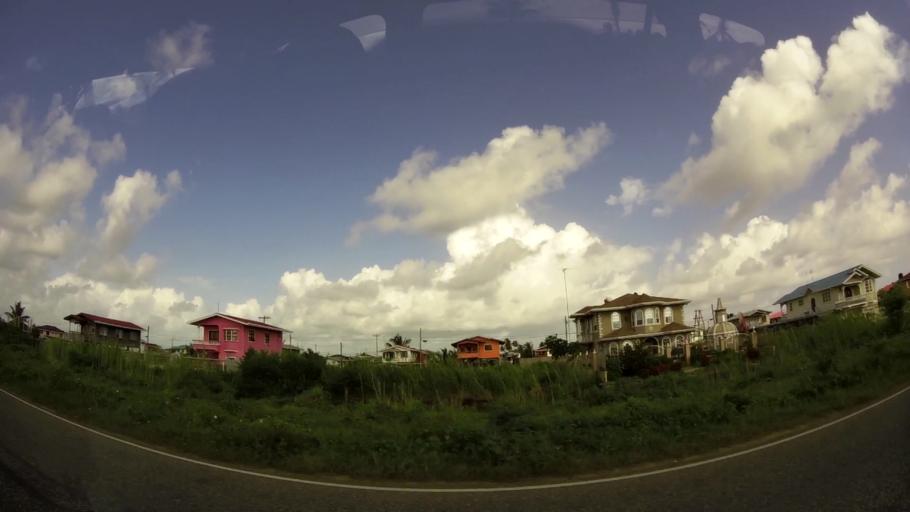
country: GY
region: Demerara-Mahaica
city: Mahaica Village
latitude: 6.7418
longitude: -57.9562
